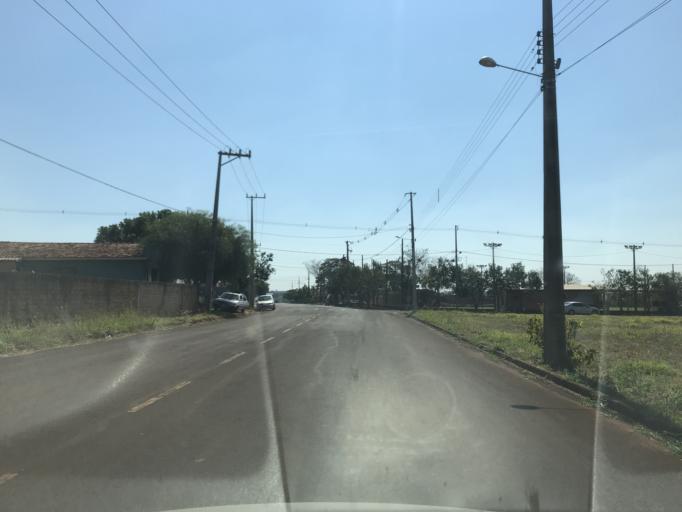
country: BR
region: Parana
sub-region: Palotina
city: Palotina
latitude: -24.2972
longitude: -53.8318
